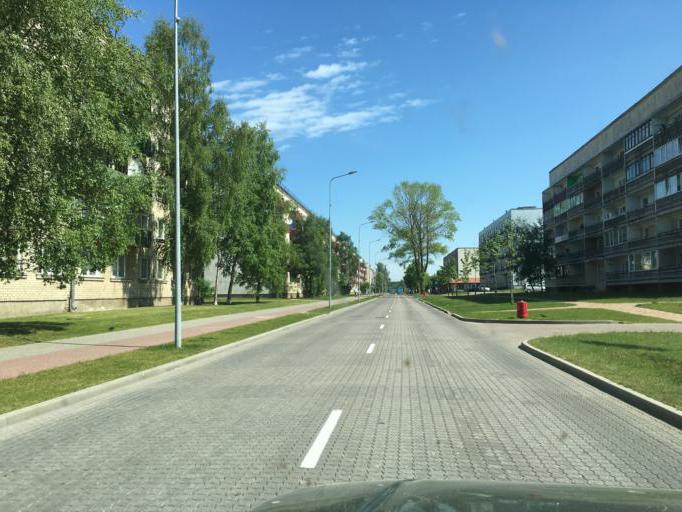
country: LV
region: Ventspils
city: Ventspils
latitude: 57.3997
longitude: 21.6083
